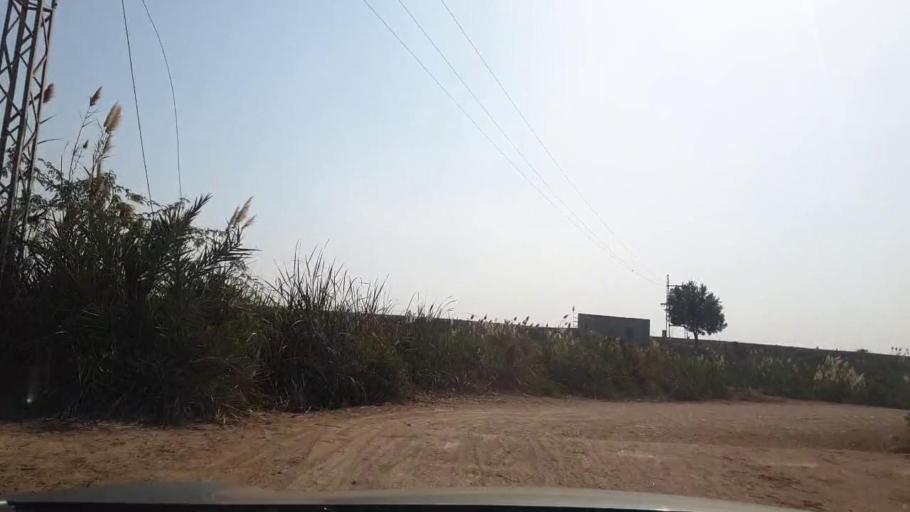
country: PK
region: Sindh
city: Mirpur Khas
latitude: 25.6431
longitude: 68.9104
